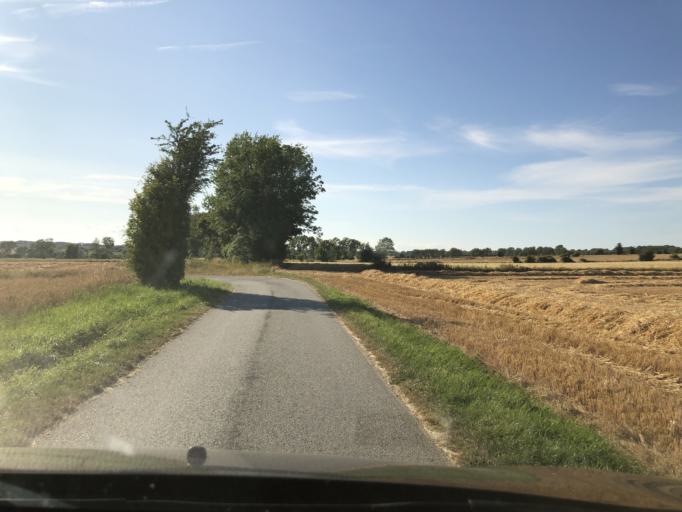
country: DK
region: South Denmark
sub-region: AEro Kommune
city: AEroskobing
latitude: 54.8550
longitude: 10.3749
